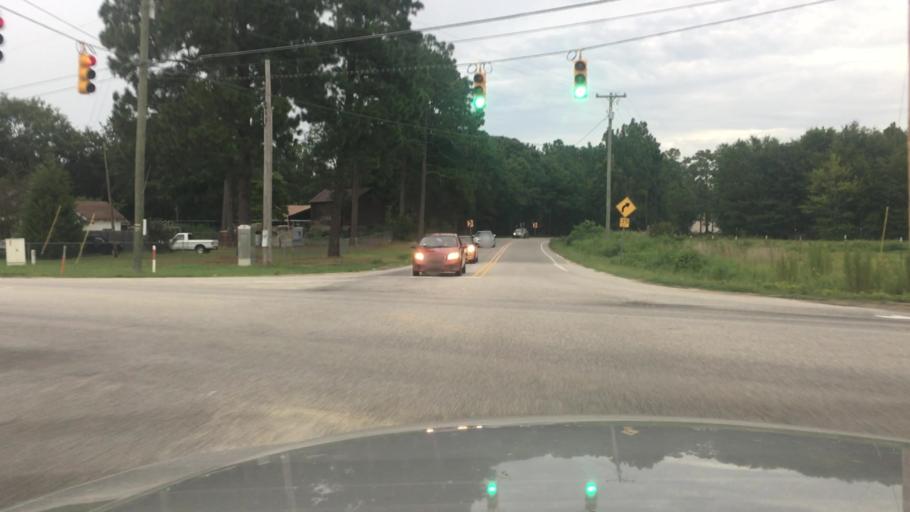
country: US
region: North Carolina
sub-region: Hoke County
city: Rockfish
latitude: 34.9881
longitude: -79.0281
